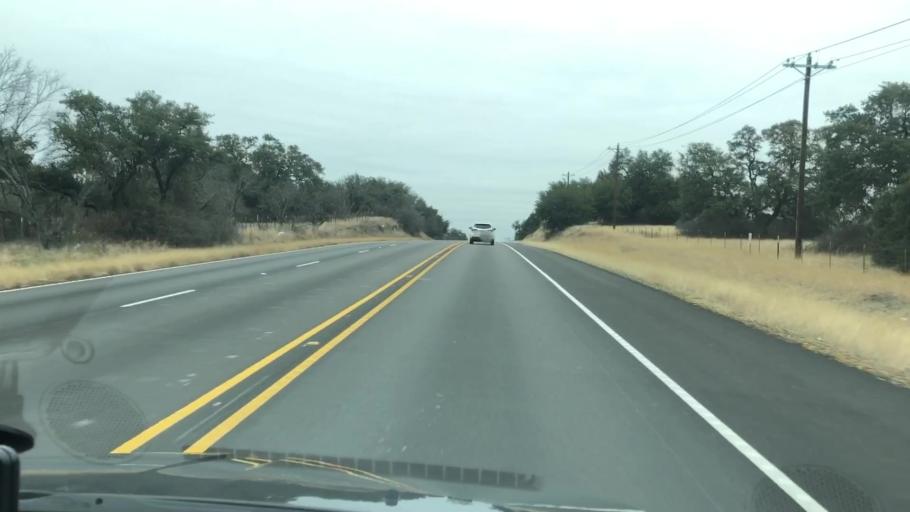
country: US
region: Texas
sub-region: Erath County
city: Stephenville
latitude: 32.3043
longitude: -98.1866
